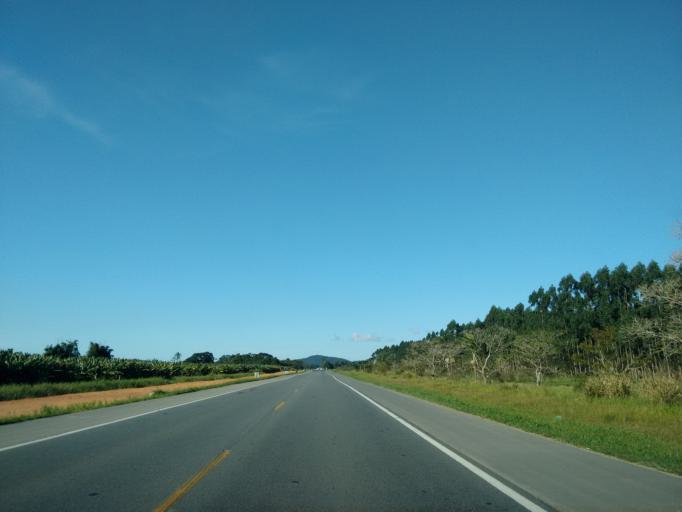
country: BR
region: Santa Catarina
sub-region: Guaramirim
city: Guaramirim
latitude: -26.4507
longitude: -48.8646
